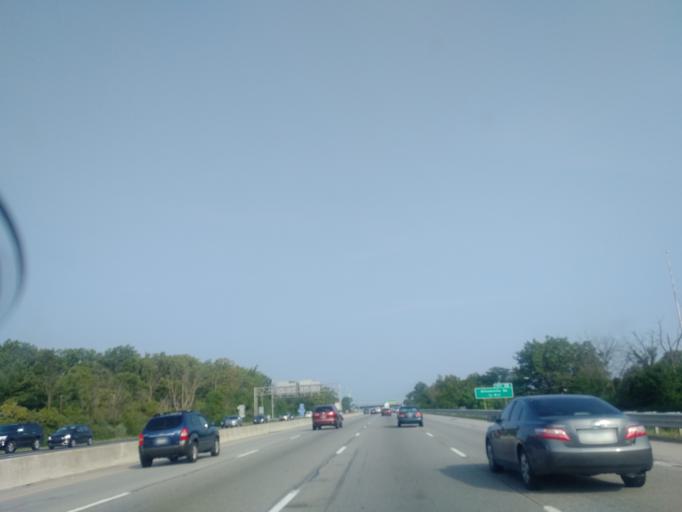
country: US
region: Indiana
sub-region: Marion County
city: Lawrence
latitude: 39.9006
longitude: -86.0628
